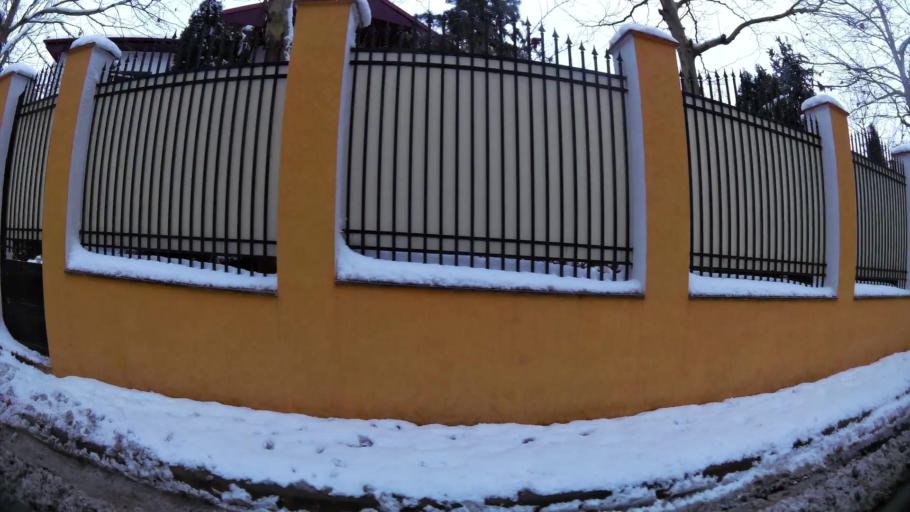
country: RO
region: Ilfov
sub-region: Comuna Tunari
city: Tunari
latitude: 44.5163
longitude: 26.1479
